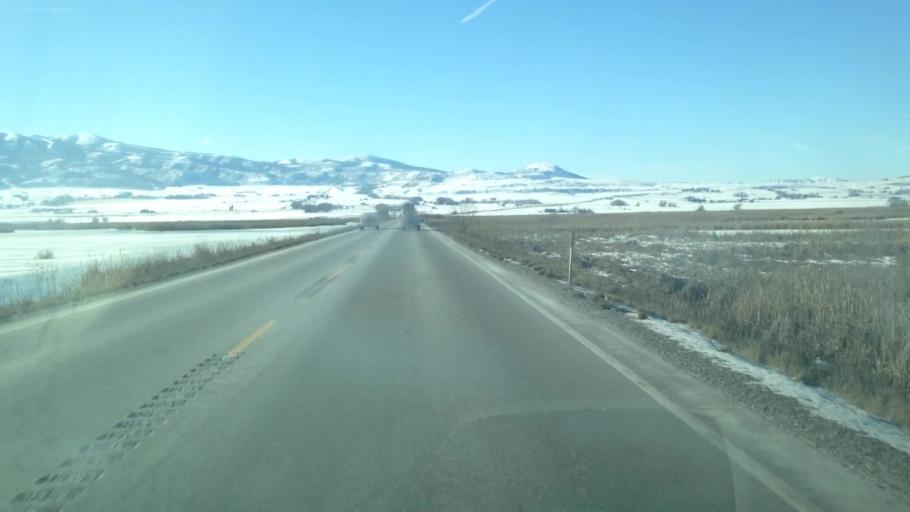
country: US
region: Utah
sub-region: Cache County
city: Benson
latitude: 41.7460
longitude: -111.9415
